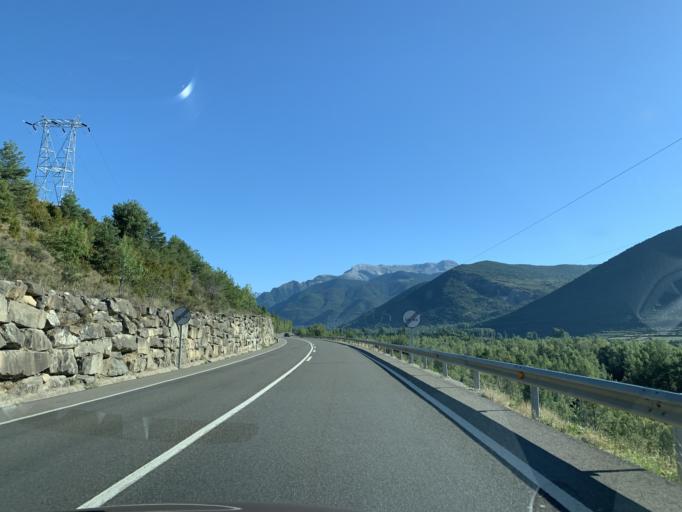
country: ES
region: Aragon
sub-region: Provincia de Huesca
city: Biescas
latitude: 42.5698
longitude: -0.3256
